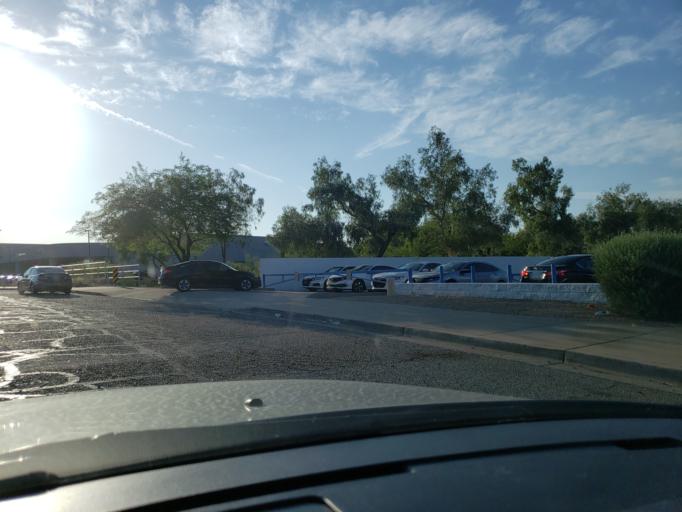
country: US
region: Arizona
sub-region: Maricopa County
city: Glendale
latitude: 33.6389
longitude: -112.0843
